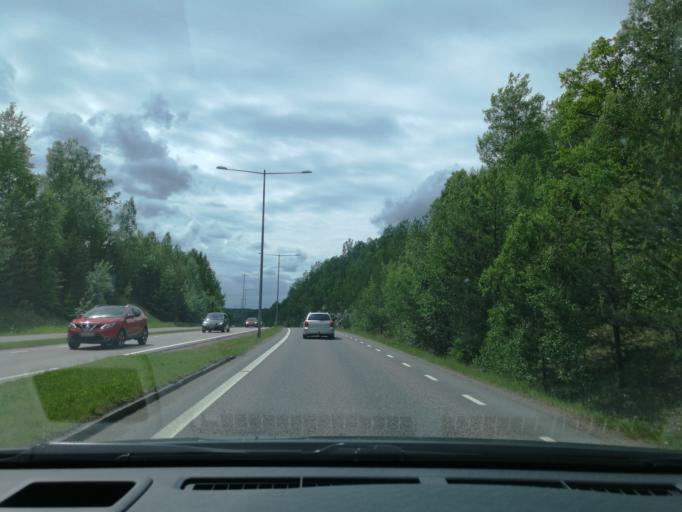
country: SE
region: Vaestmanland
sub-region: Vasteras
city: Vasteras
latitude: 59.6376
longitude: 16.5096
